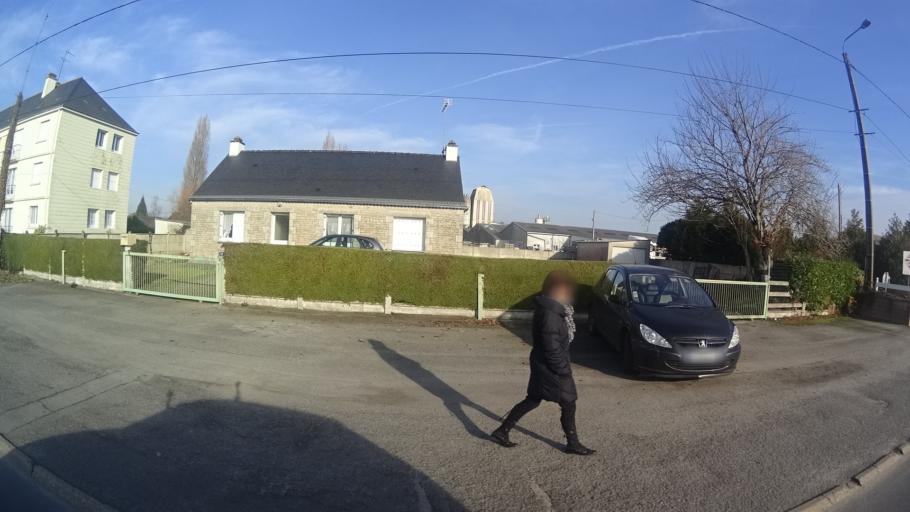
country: FR
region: Brittany
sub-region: Departement du Morbihan
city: Allaire
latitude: 47.6358
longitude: -2.1588
